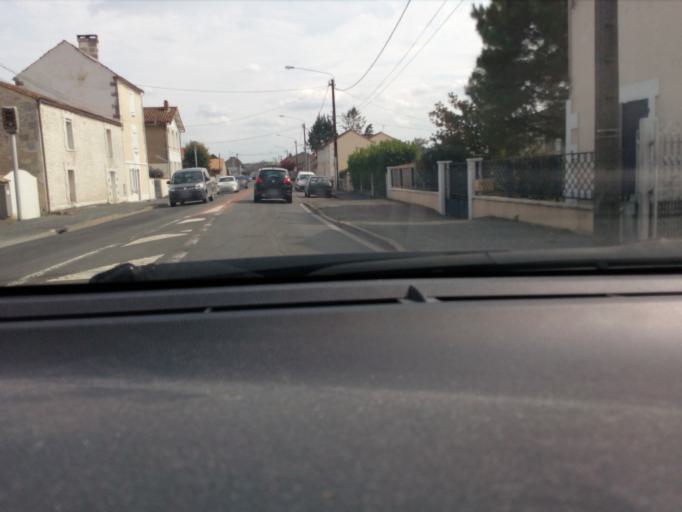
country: FR
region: Poitou-Charentes
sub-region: Departement de la Charente
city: Saint-Yrieix-sur-Charente
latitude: 45.6693
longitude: 0.1179
